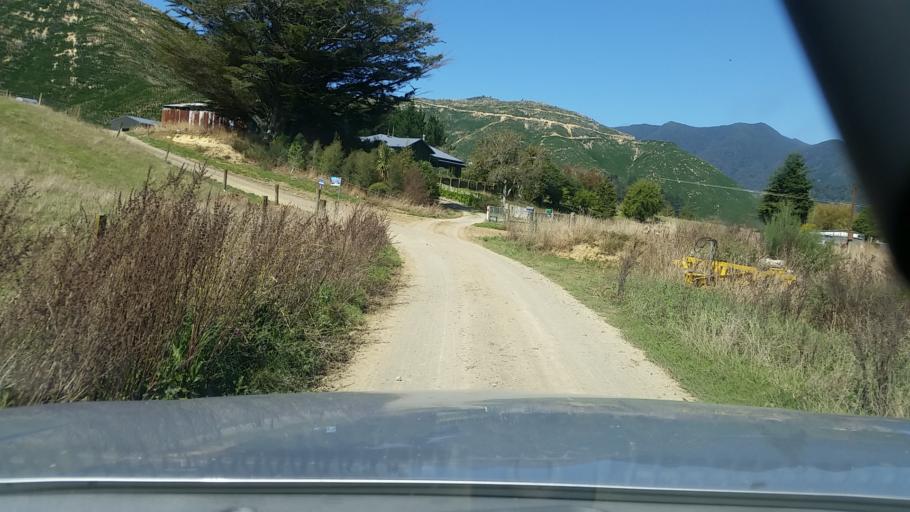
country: NZ
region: Nelson
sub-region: Nelson City
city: Nelson
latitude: -41.2718
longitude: 173.5801
